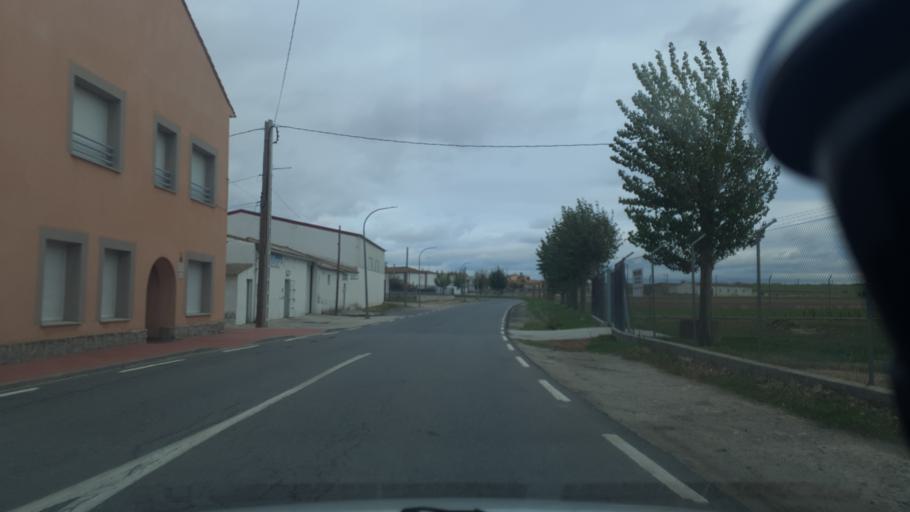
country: ES
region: Castille and Leon
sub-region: Provincia de Avila
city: Velayos
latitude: 40.8391
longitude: -4.6251
